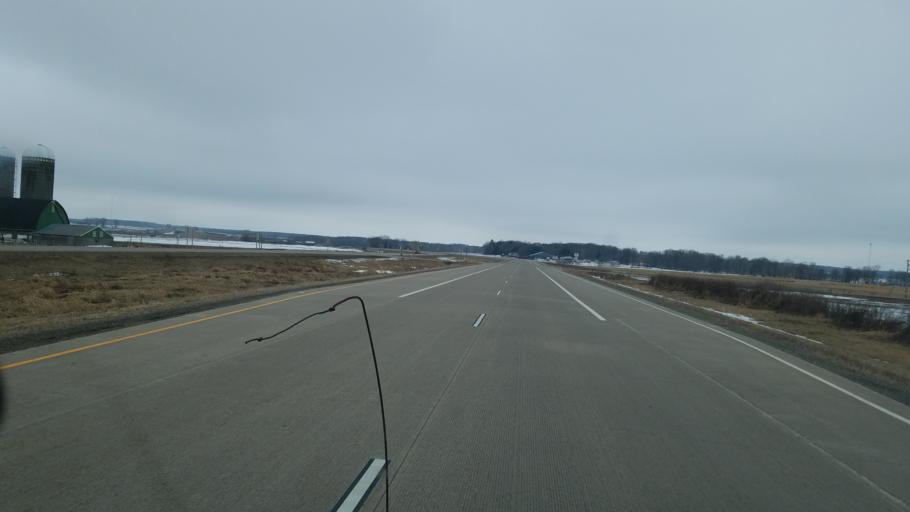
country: US
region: Wisconsin
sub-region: Marathon County
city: Stratford
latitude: 44.6197
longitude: -89.9144
